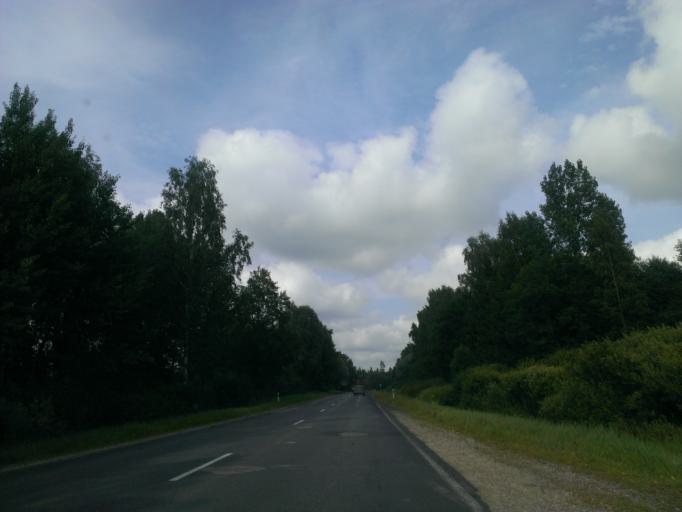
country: LV
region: Amatas Novads
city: Drabesi
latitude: 57.2493
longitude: 25.3345
